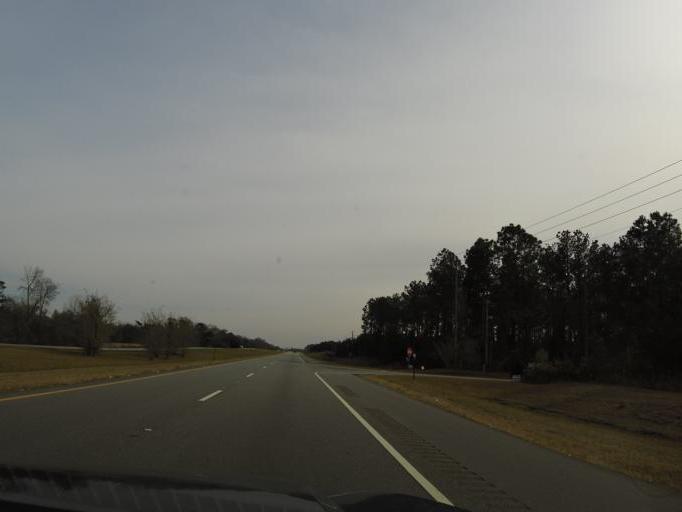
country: US
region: Georgia
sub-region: Seminole County
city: Donalsonville
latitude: 31.1125
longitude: -85.0320
